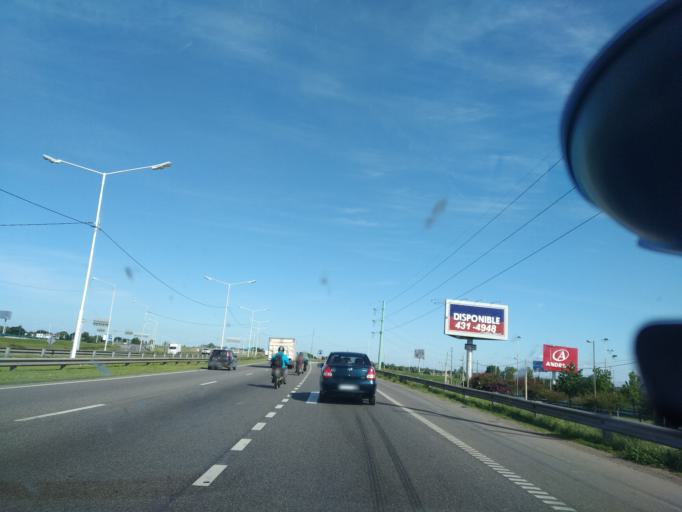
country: AR
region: Santa Fe
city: Gobernador Galvez
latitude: -33.0131
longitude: -60.6685
